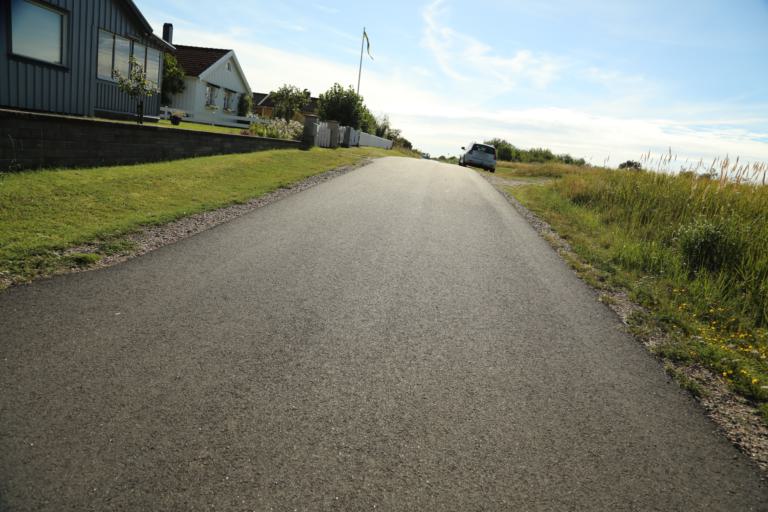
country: SE
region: Halland
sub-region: Varbergs Kommun
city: Traslovslage
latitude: 57.0811
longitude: 12.2701
